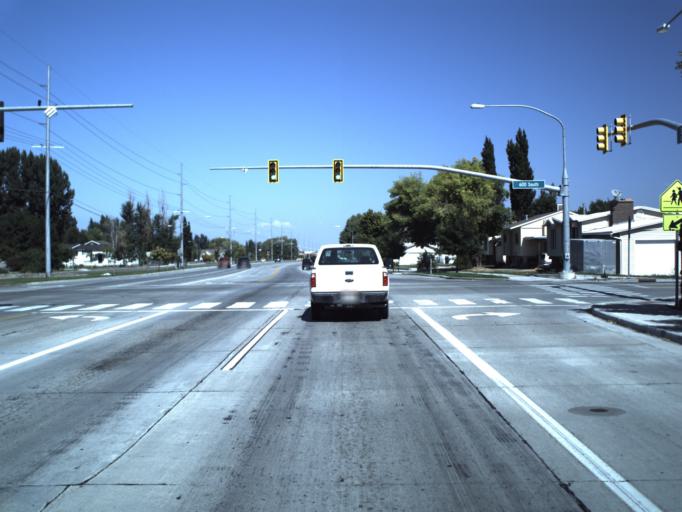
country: US
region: Utah
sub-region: Cache County
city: Logan
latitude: 41.7204
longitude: -111.8599
